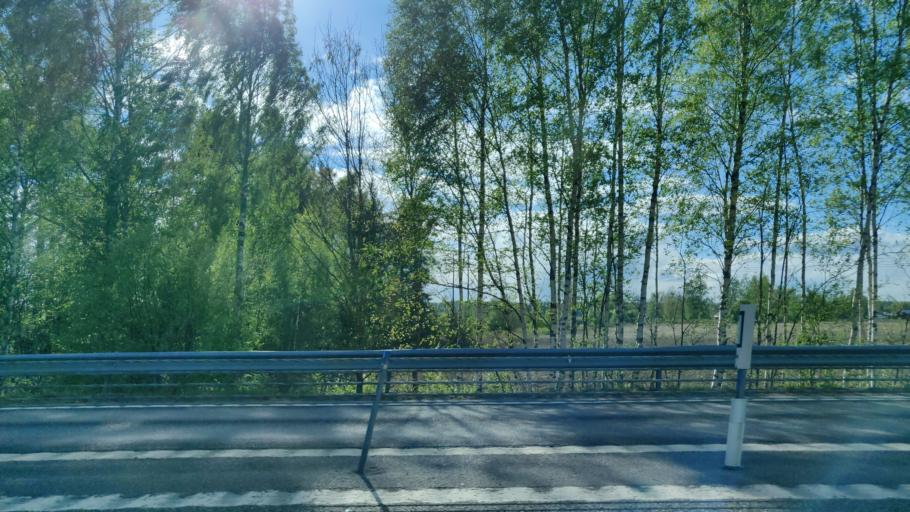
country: SE
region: Vaermland
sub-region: Forshaga Kommun
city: Forshaga
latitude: 59.4629
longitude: 13.4162
